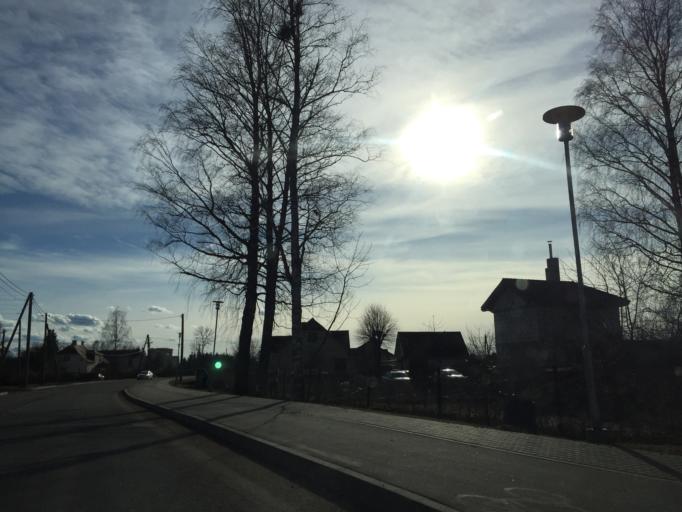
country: LV
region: Sigulda
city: Sigulda
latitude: 57.1588
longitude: 24.8810
